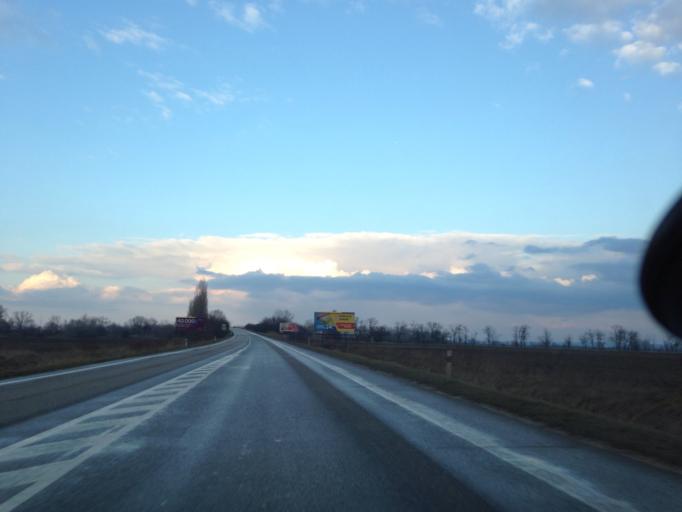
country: SK
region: Nitriansky
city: Komarno
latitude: 47.7720
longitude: 18.1569
